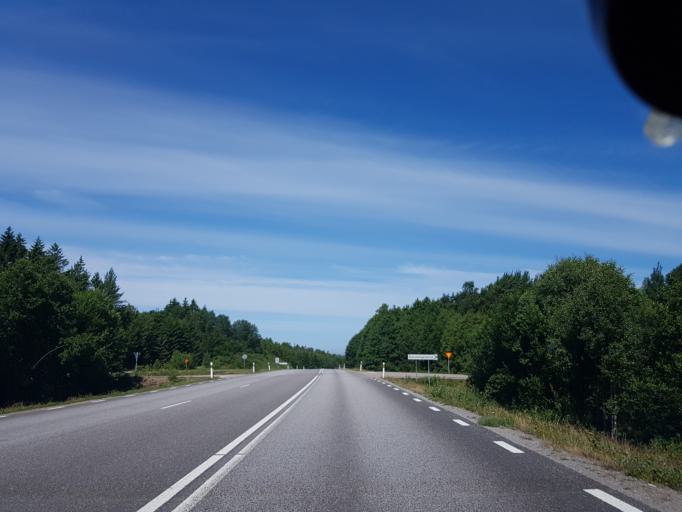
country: SE
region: Vaestra Goetaland
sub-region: Lysekils Kommun
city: Lysekil
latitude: 58.1600
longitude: 11.4976
